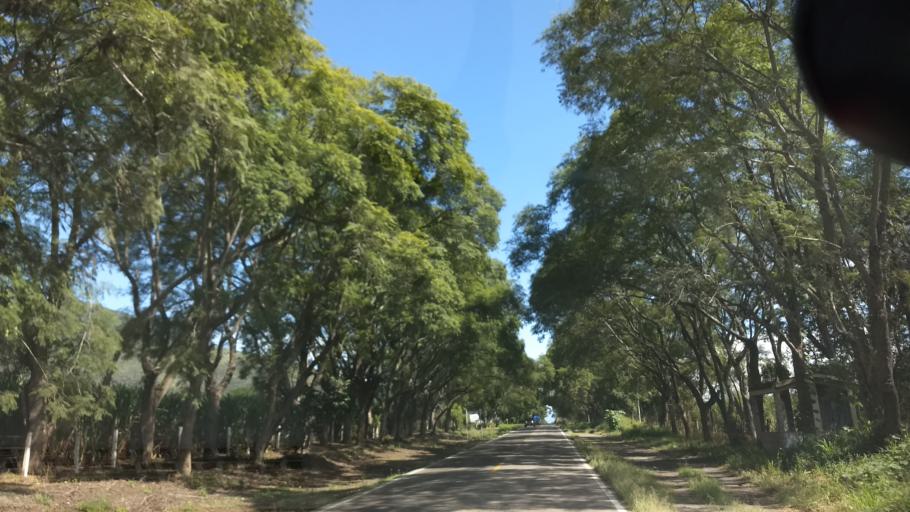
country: MX
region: Jalisco
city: Tuxpan
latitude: 19.5359
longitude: -103.4134
